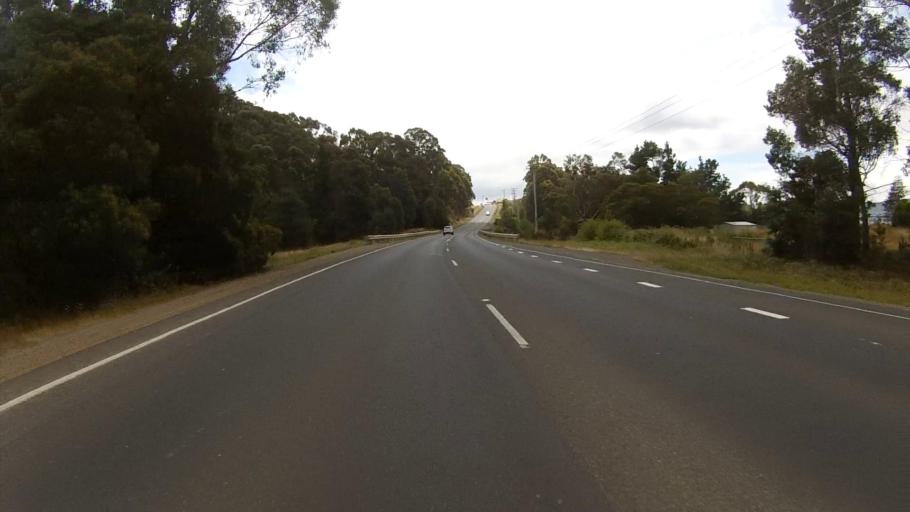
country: AU
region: Tasmania
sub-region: Kingborough
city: Margate
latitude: -43.0737
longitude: 147.2566
